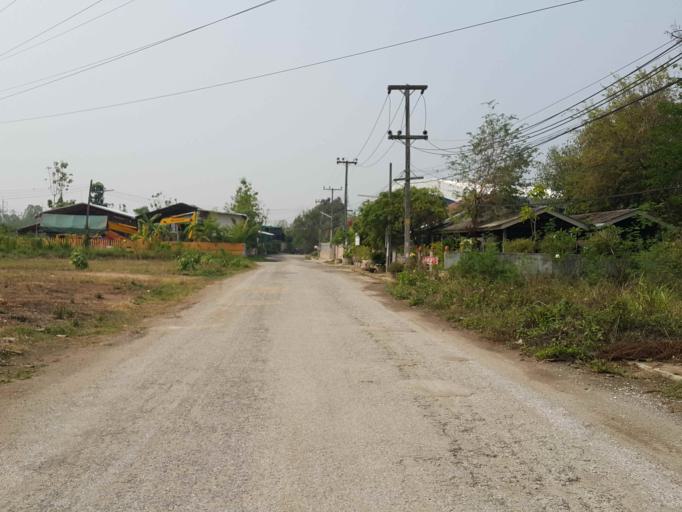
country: TH
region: Chiang Mai
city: San Kamphaeng
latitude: 18.7653
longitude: 99.0647
